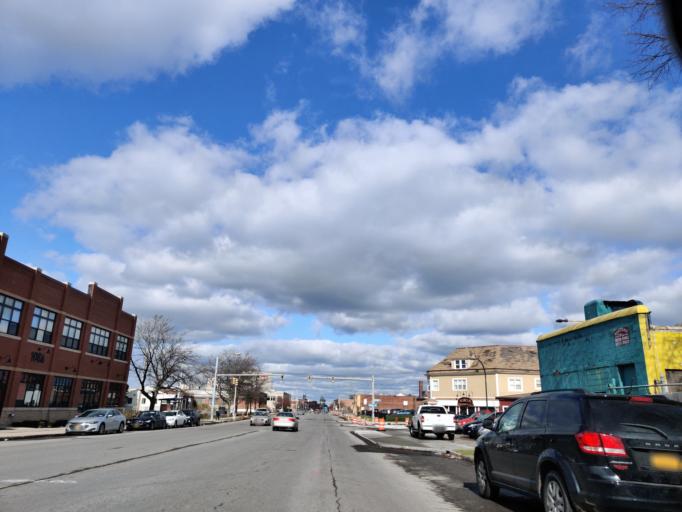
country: US
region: New York
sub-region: Erie County
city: Buffalo
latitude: 42.9123
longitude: -78.8998
